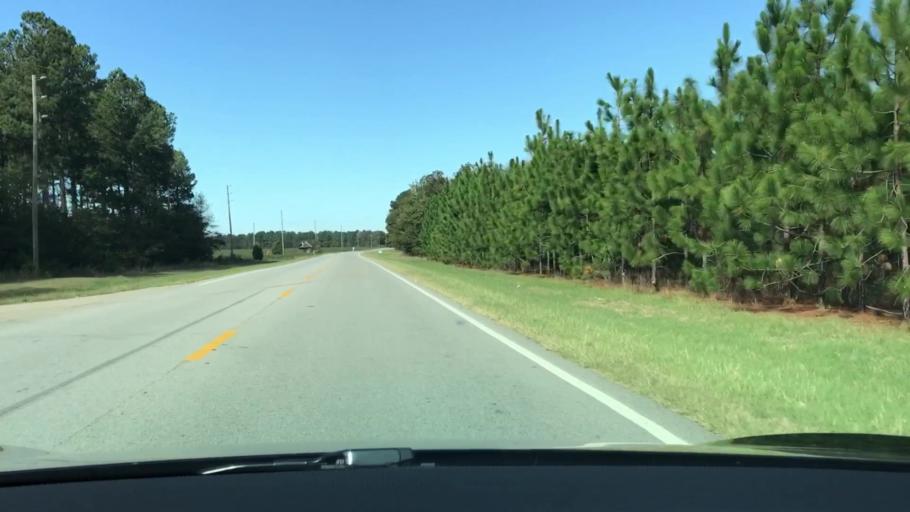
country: US
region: Georgia
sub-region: Glascock County
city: Gibson
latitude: 33.3101
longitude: -82.5362
